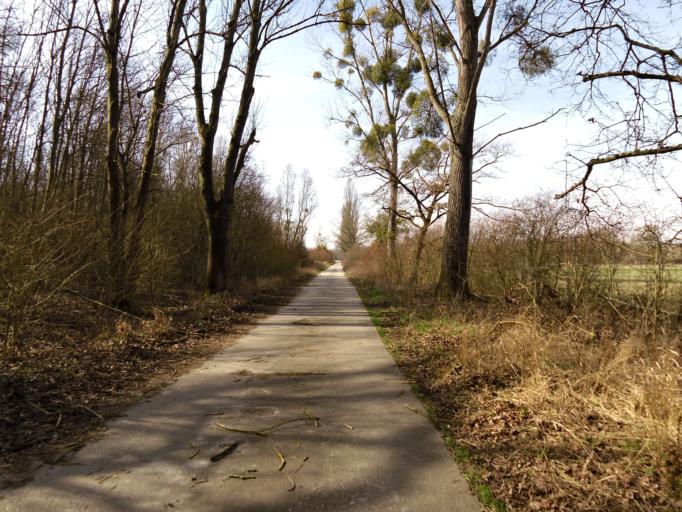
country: DE
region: Hesse
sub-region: Regierungsbezirk Darmstadt
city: Stockstadt am Rhein
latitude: 49.8161
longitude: 8.4350
